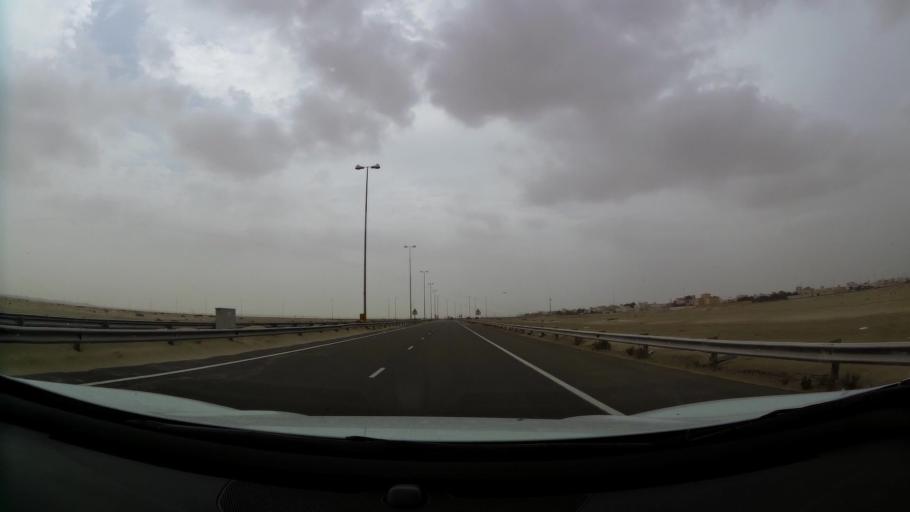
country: AE
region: Abu Dhabi
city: Abu Dhabi
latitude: 24.3632
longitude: 54.6686
